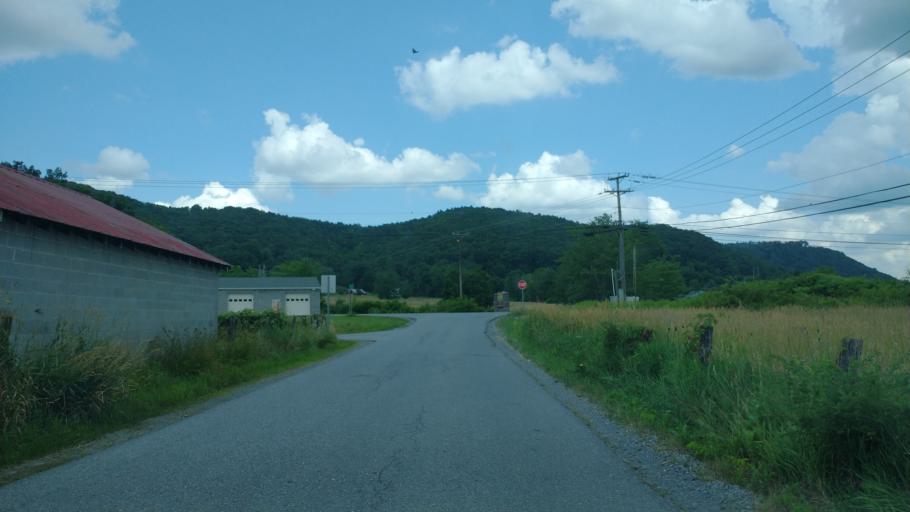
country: US
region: West Virginia
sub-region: Mercer County
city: Athens
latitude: 37.4564
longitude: -81.0109
